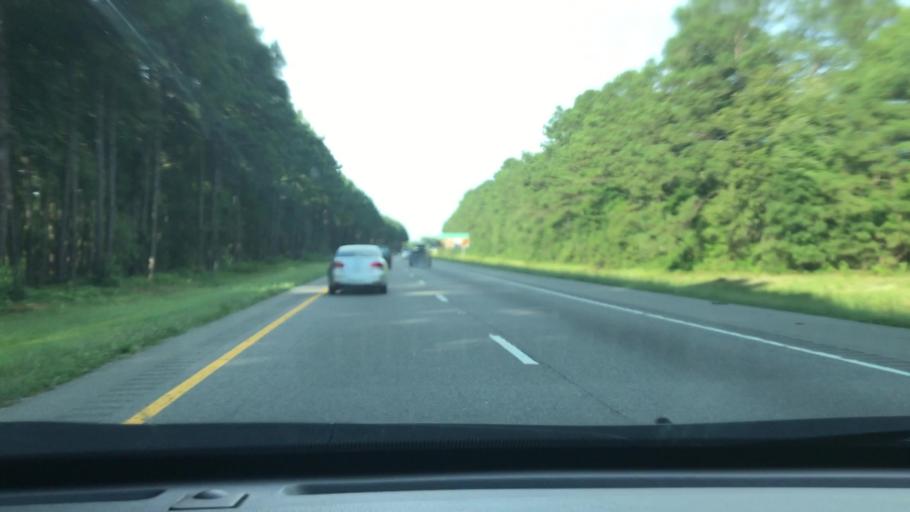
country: US
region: North Carolina
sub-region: Robeson County
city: Fairmont
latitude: 34.5815
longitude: -79.1418
